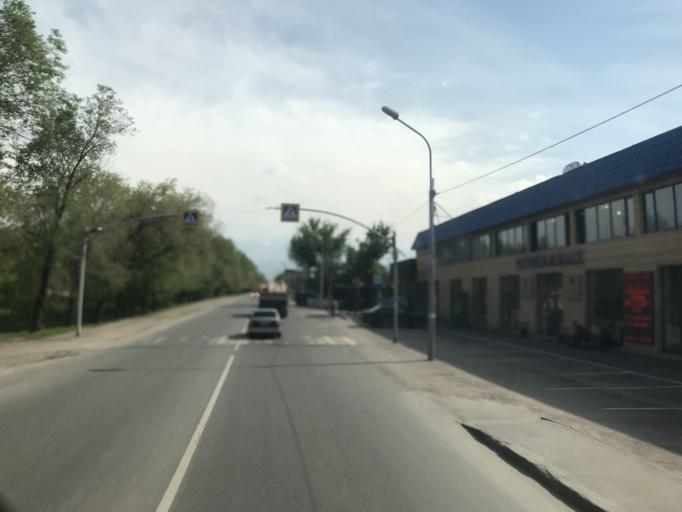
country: KZ
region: Almaty Oblysy
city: Burunday
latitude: 43.2478
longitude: 76.8037
